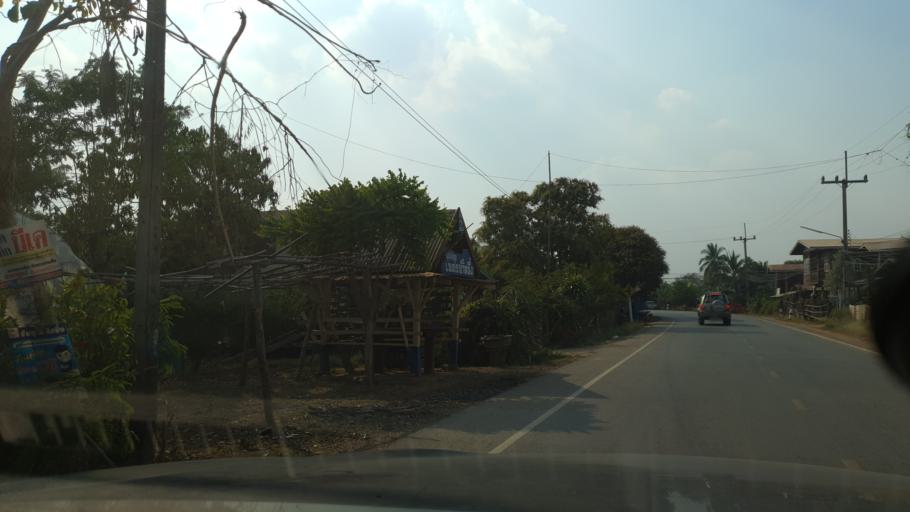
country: TH
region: Sukhothai
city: Ban Dan Lan Hoi
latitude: 17.1138
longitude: 99.5441
